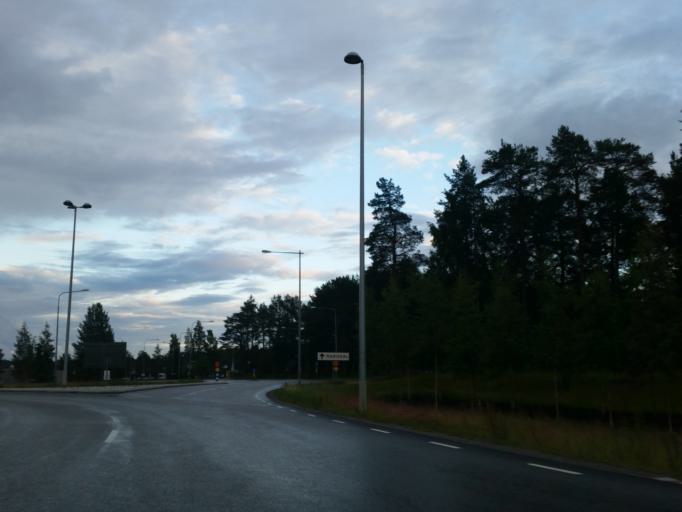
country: SE
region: Vaesterbotten
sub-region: Umea Kommun
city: Ersmark
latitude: 63.8491
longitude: 20.2953
